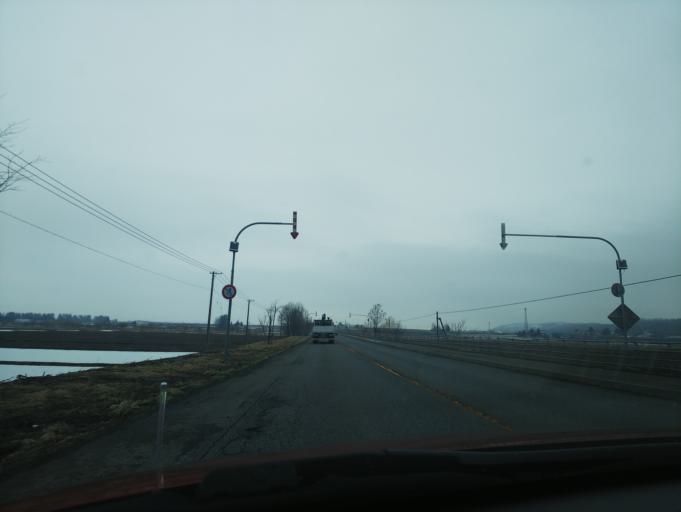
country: JP
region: Hokkaido
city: Nayoro
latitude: 44.0651
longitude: 142.3987
